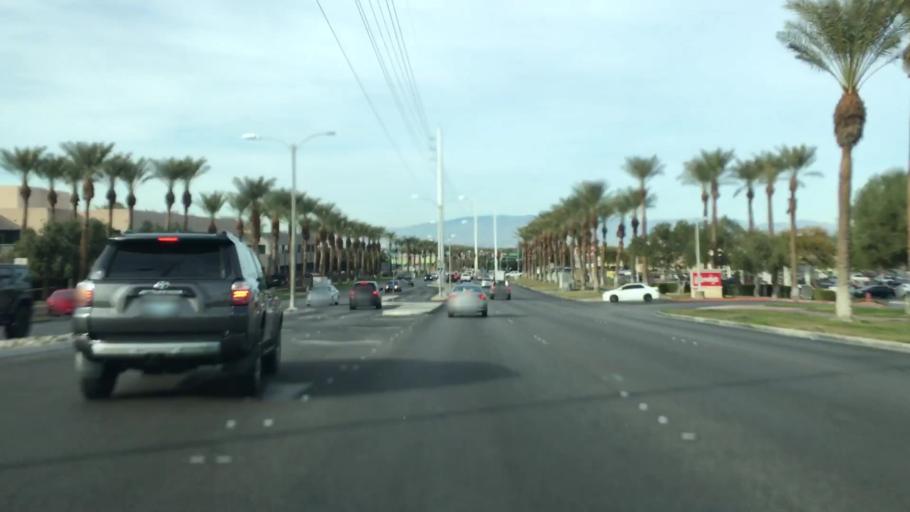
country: US
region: Nevada
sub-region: Clark County
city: Whitney
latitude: 36.0259
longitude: -115.0853
